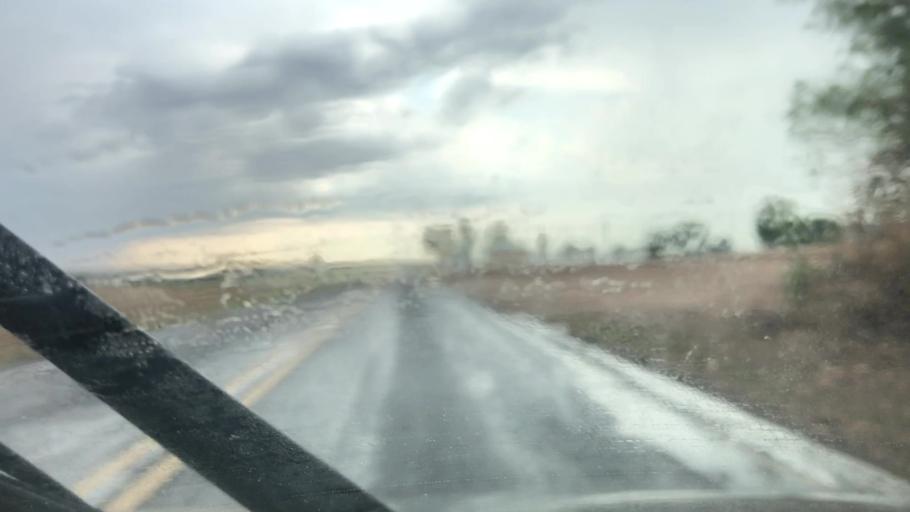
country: US
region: New Mexico
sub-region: Dona Ana County
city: Vado
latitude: 32.0690
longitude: -106.6808
